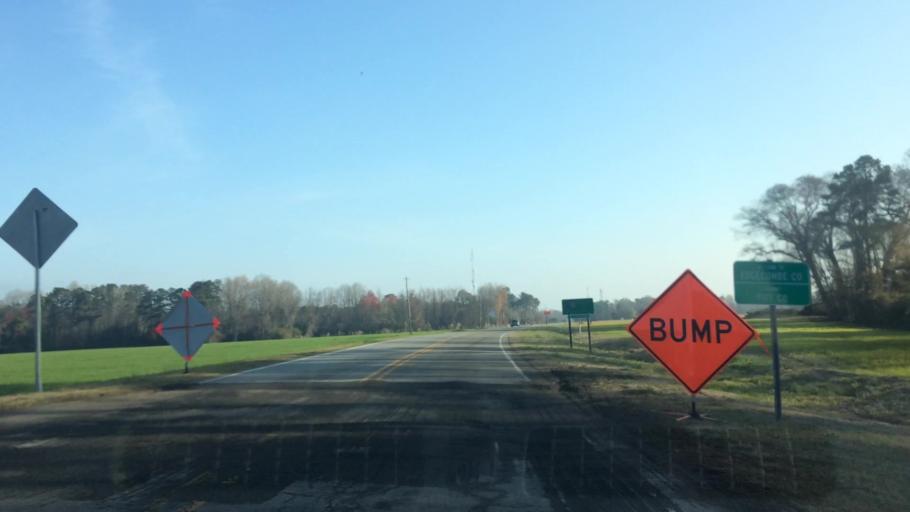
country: US
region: North Carolina
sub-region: Edgecombe County
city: Pinetops
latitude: 35.6870
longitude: -77.6433
